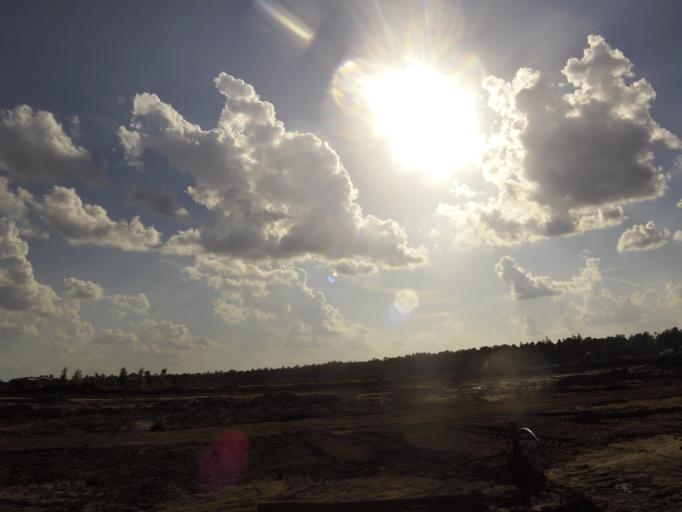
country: US
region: Florida
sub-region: Clay County
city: Green Cove Springs
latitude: 30.0327
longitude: -81.6288
